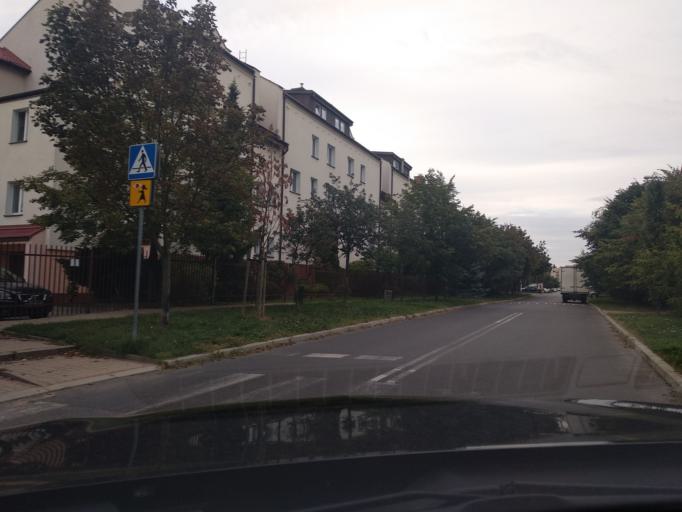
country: PL
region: Masovian Voivodeship
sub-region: Warszawa
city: Ursynow
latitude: 52.1280
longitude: 21.0558
